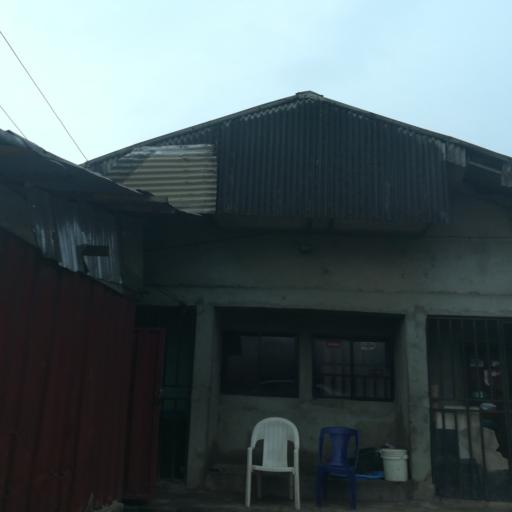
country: NG
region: Rivers
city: Port Harcourt
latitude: 4.7584
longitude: 7.0113
